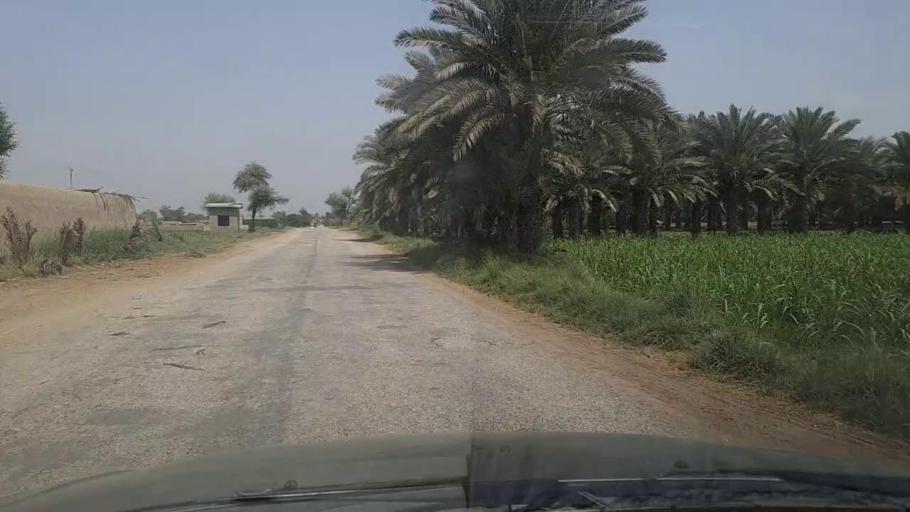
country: PK
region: Sindh
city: Setharja Old
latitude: 27.1627
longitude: 68.5180
